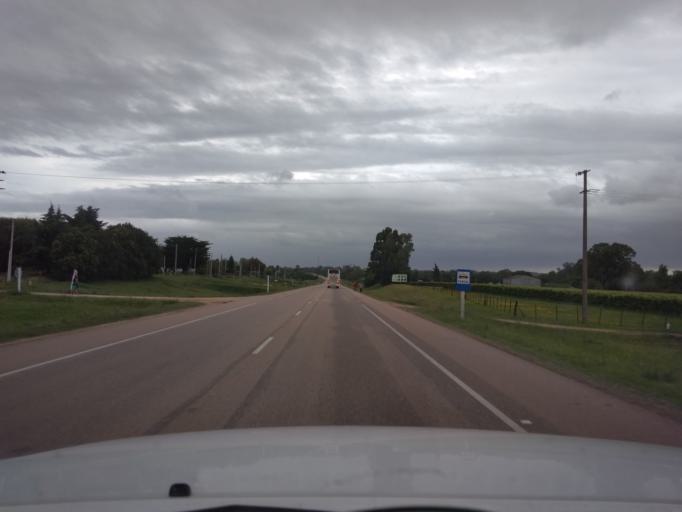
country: UY
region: Canelones
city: Canelones
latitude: -34.4920
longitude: -56.2819
